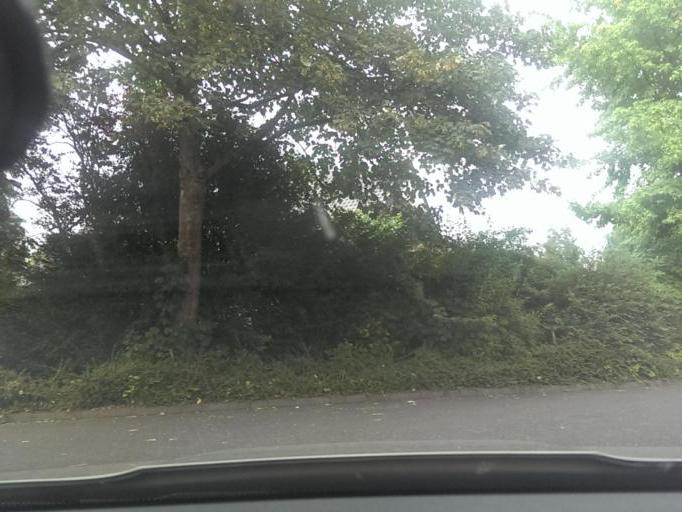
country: DE
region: North Rhine-Westphalia
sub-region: Regierungsbezirk Detmold
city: Delbruck
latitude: 51.7675
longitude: 8.5490
